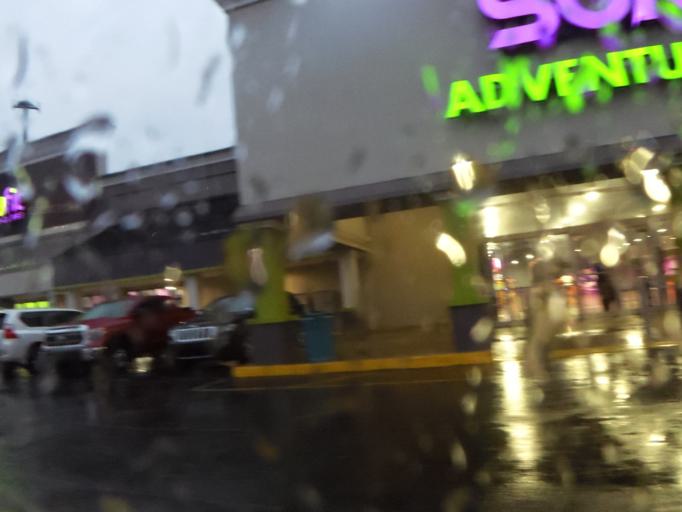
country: US
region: Florida
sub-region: Duval County
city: Jacksonville
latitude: 30.3208
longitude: -81.5571
